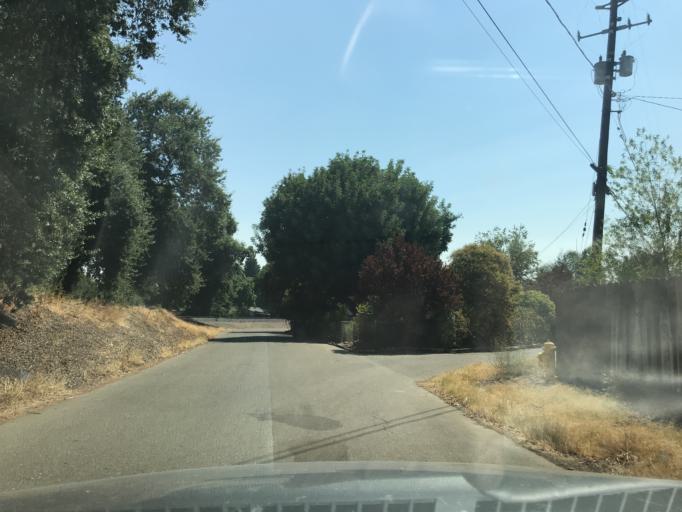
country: US
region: California
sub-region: Merced County
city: Merced
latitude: 37.3138
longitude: -120.4960
